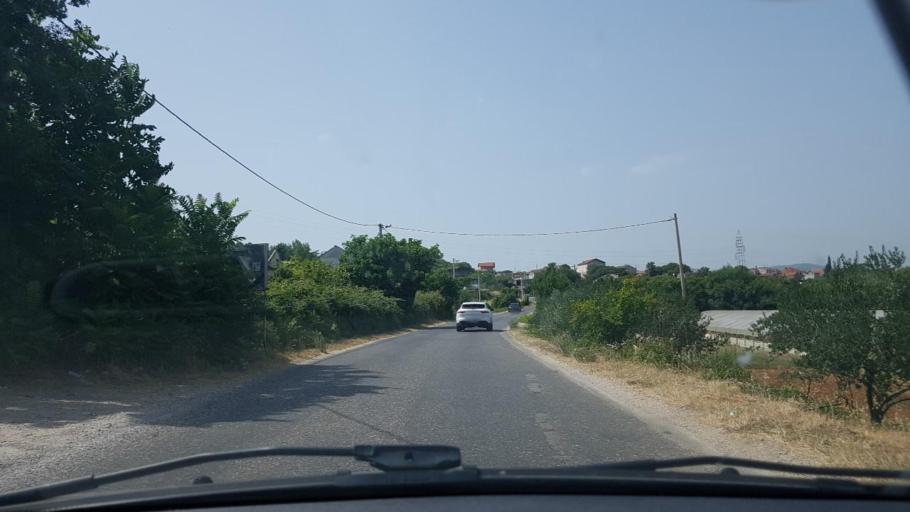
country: HR
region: Dubrovacko-Neretvanska
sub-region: Grad Dubrovnik
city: Metkovic
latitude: 43.0466
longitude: 17.7042
